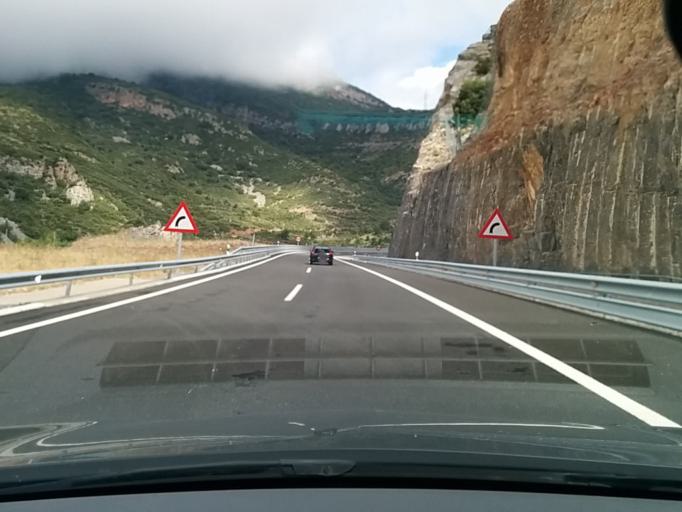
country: ES
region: Aragon
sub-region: Provincia de Huesca
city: Nueno
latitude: 42.2825
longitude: -0.4238
